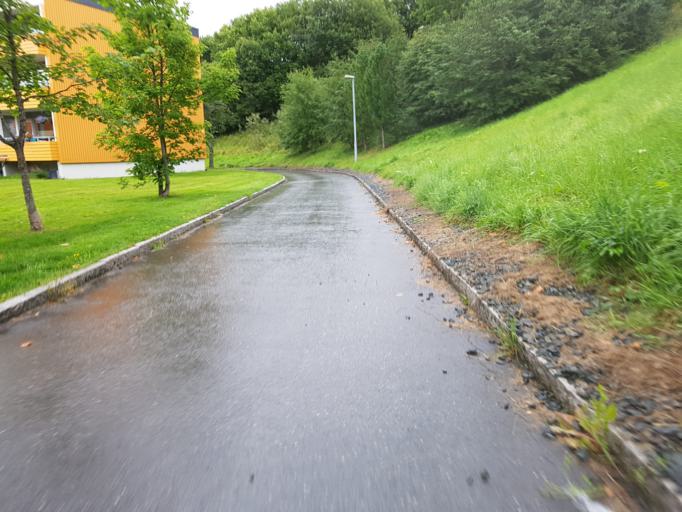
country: NO
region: Sor-Trondelag
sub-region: Trondheim
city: Trondheim
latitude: 63.4007
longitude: 10.4394
